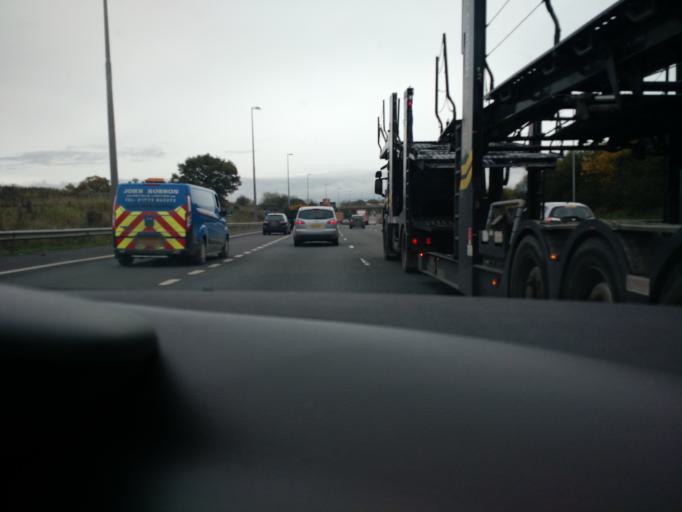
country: GB
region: England
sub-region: Lancashire
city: Goosnargh
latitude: 53.7885
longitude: -2.6572
